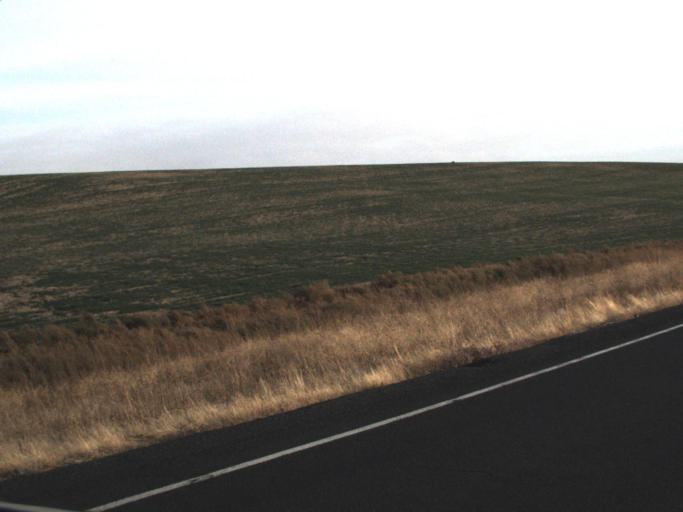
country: US
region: Washington
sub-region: Adams County
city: Ritzville
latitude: 47.1868
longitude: -118.6870
